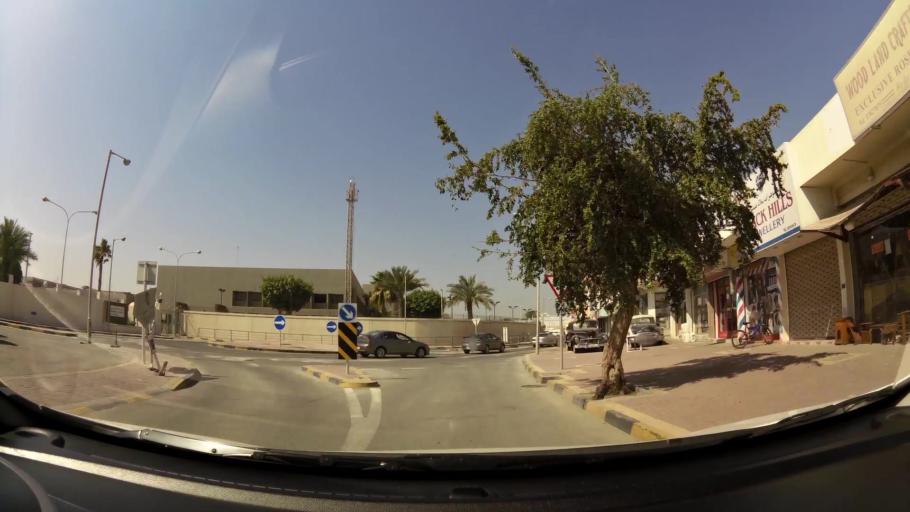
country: BH
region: Manama
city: Manama
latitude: 26.2098
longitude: 50.6046
